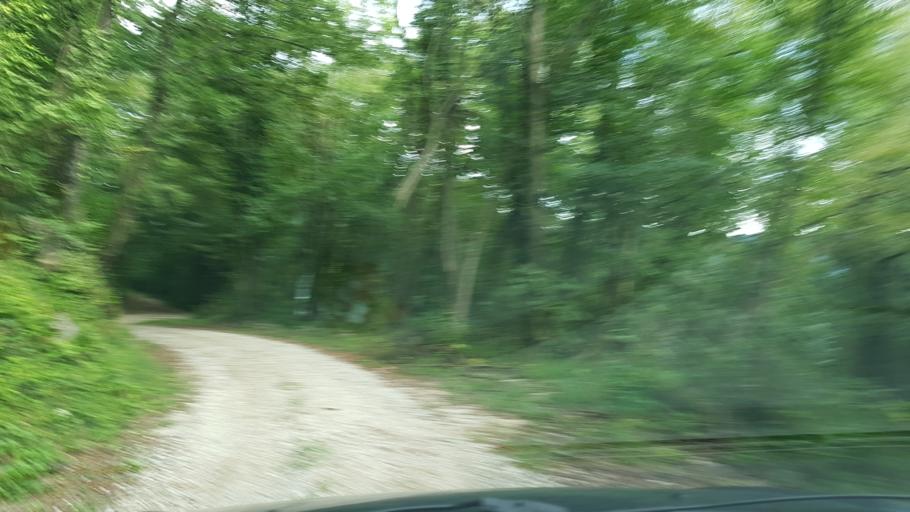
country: SI
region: Kanal
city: Deskle
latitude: 46.0543
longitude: 13.5878
